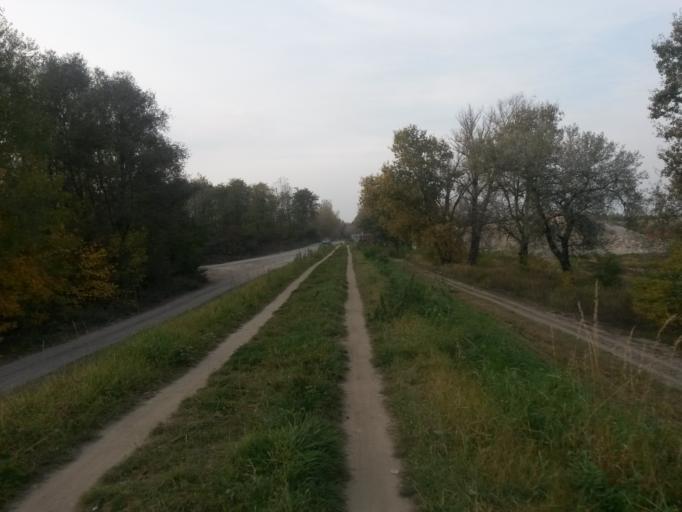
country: PL
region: Masovian Voivodeship
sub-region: Warszawa
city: Wawer
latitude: 52.1469
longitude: 21.1517
